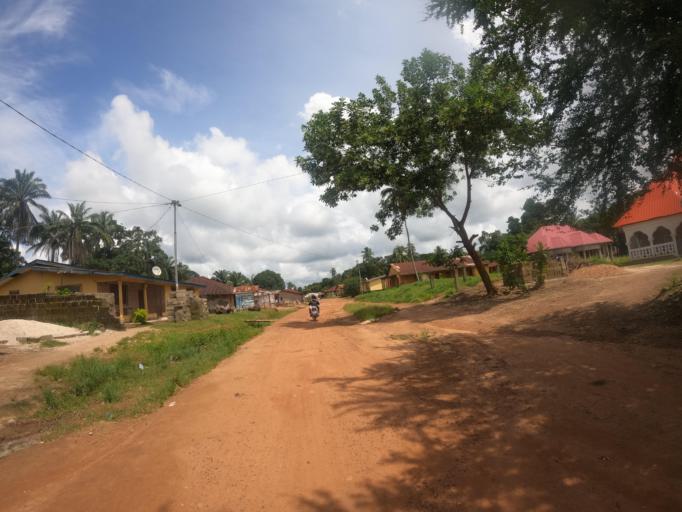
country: SL
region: Northern Province
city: Makeni
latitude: 8.8970
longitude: -12.0577
